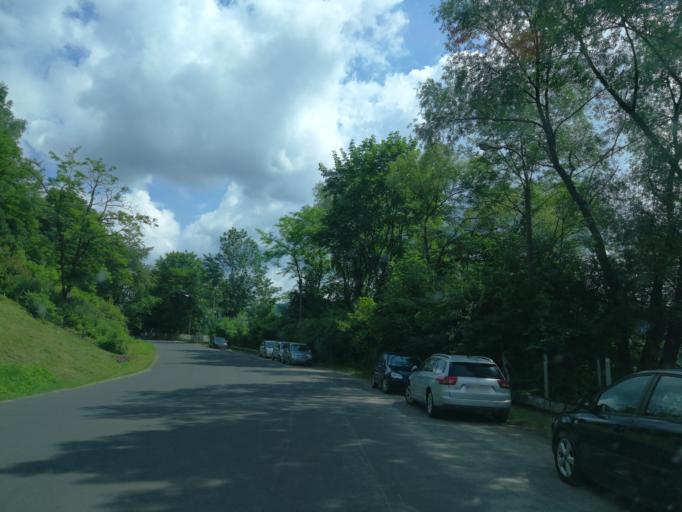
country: PL
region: Subcarpathian Voivodeship
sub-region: Powiat leski
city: Uherce Mineralne
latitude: 49.4311
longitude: 22.4123
